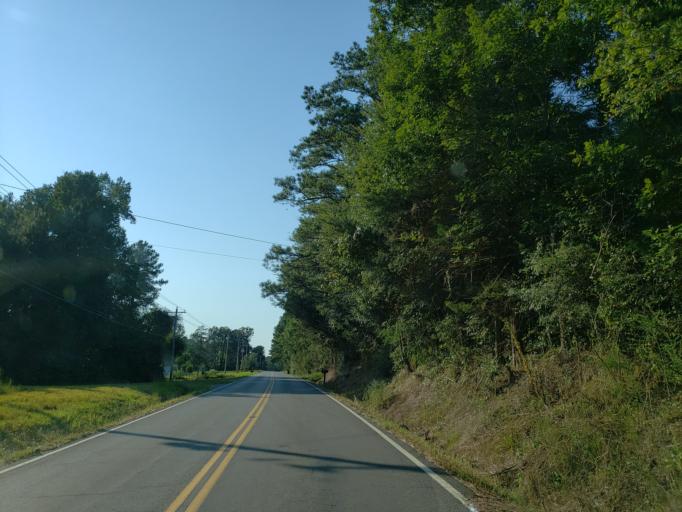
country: US
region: Tennessee
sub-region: Bradley County
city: Wildwood Lake
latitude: 35.0731
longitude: -84.7800
